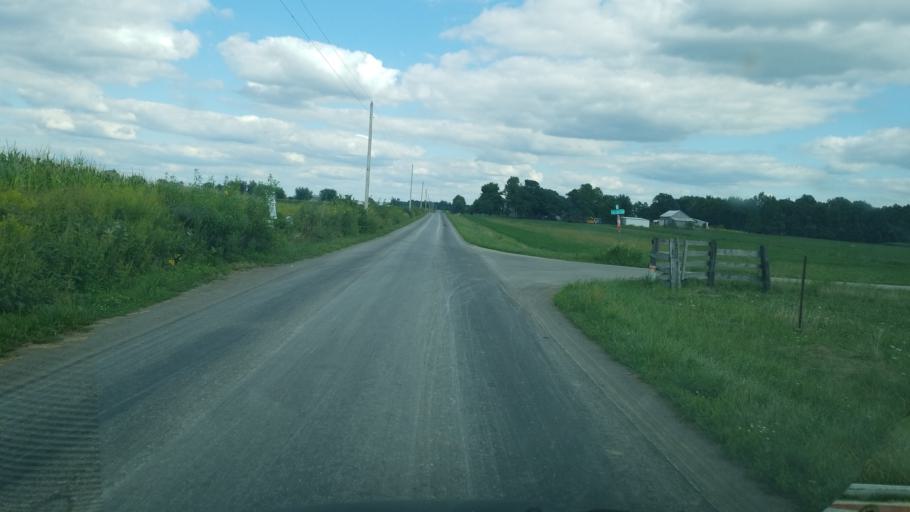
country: US
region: Ohio
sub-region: Logan County
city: De Graff
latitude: 40.3769
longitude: -83.8977
